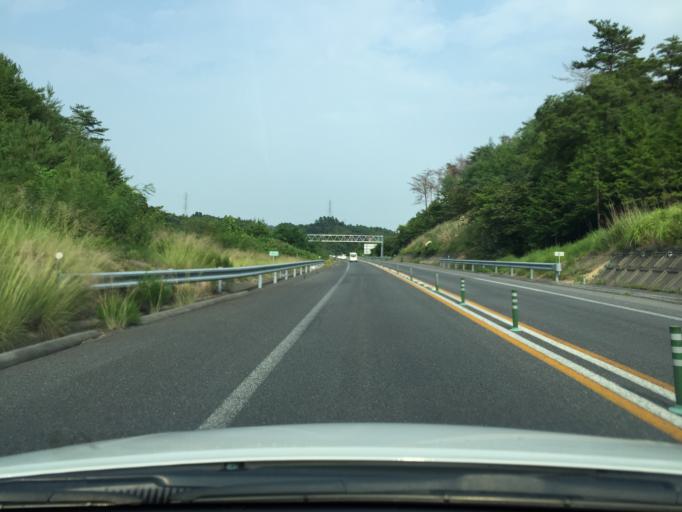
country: JP
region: Fukushima
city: Iwaki
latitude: 37.1221
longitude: 140.9293
